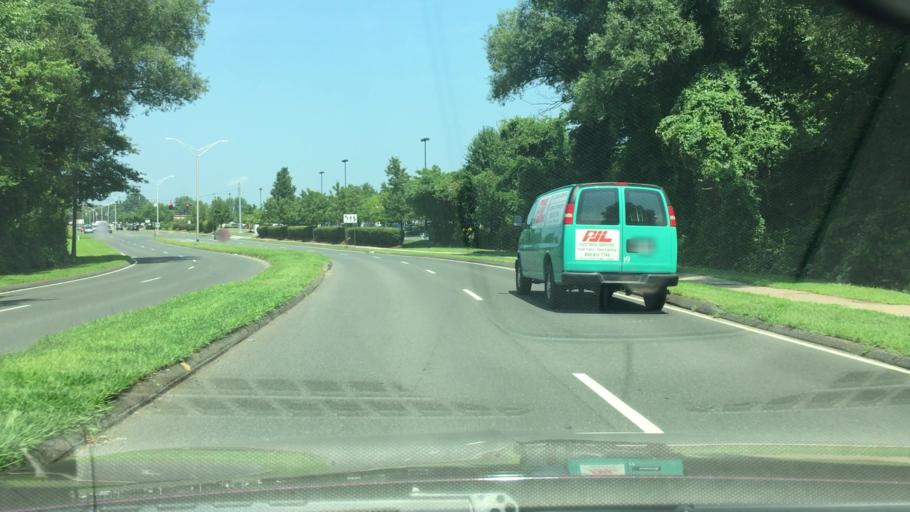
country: US
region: Connecticut
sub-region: Hartford County
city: Enfield
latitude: 41.9922
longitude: -72.5768
